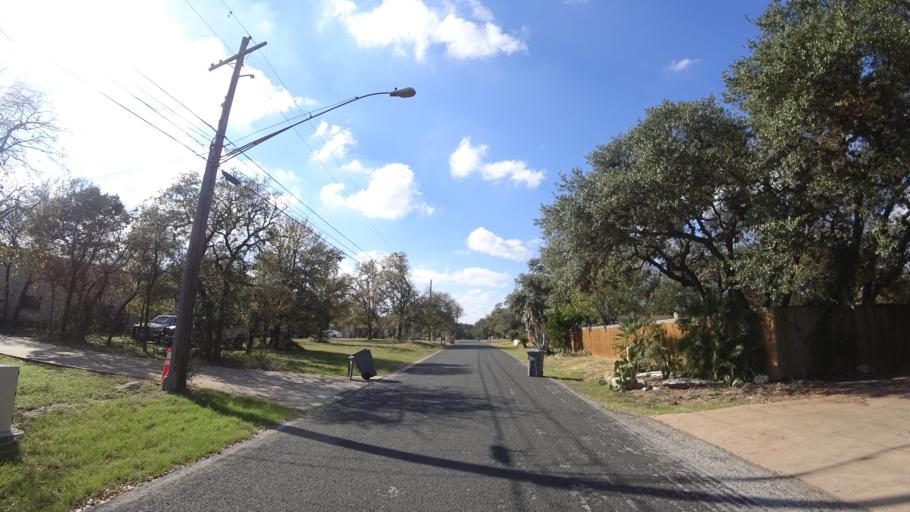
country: US
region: Texas
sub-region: Travis County
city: Shady Hollow
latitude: 30.1789
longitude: -97.8469
